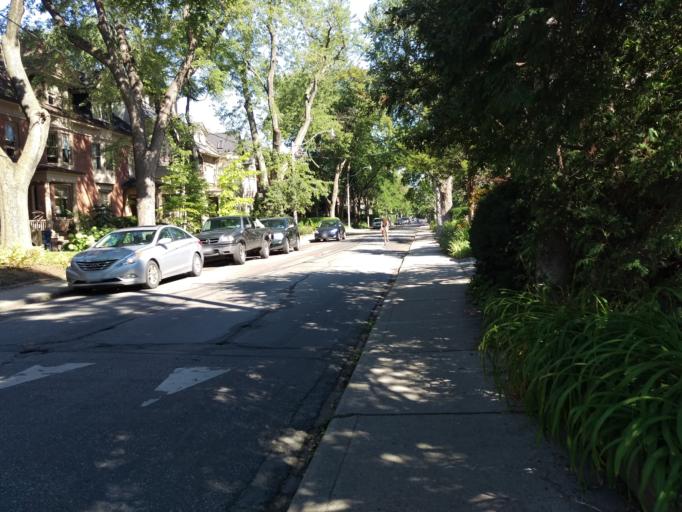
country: CA
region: Ontario
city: Toronto
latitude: 43.6670
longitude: -79.4079
